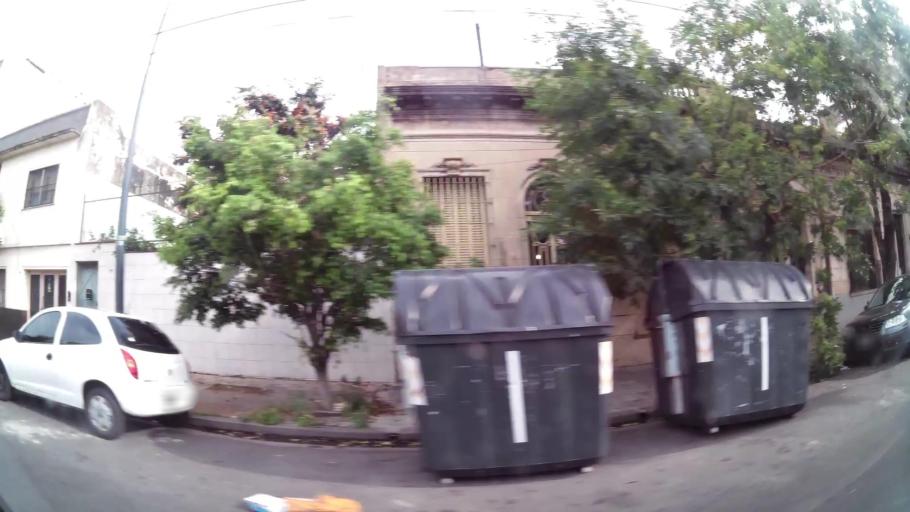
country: AR
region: Buenos Aires F.D.
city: Buenos Aires
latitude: -34.6283
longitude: -58.4187
